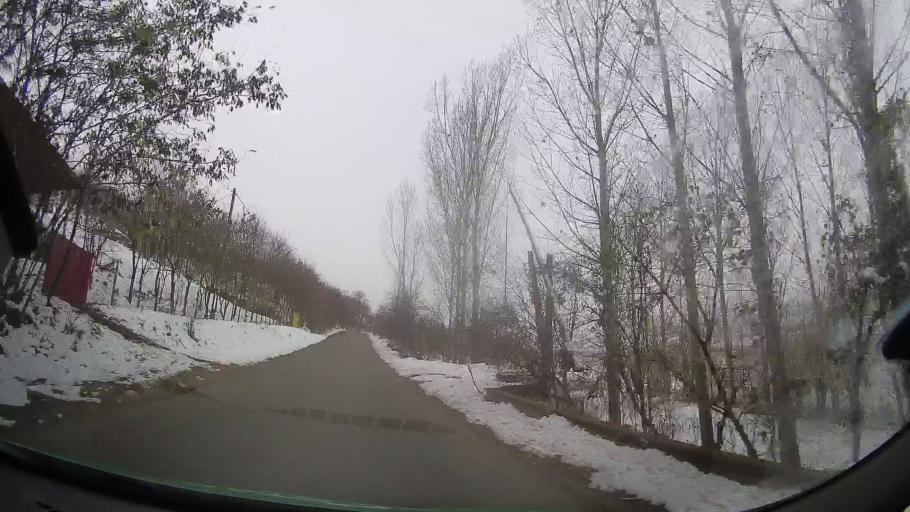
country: RO
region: Bacau
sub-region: Comuna Vultureni
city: Vultureni
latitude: 46.3561
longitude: 27.2894
